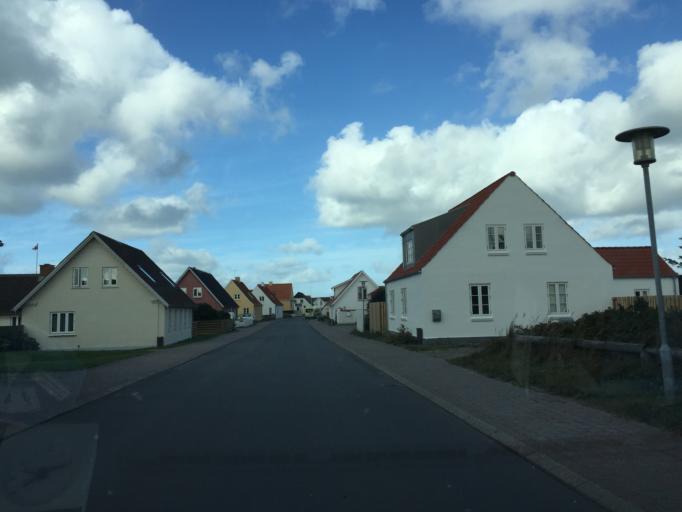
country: DK
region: North Denmark
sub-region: Thisted Kommune
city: Hanstholm
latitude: 57.0413
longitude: 8.4864
